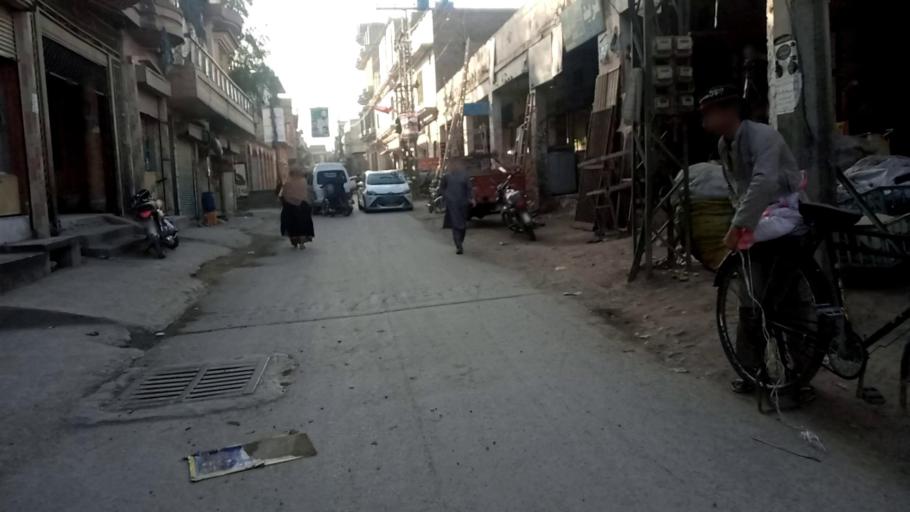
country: PK
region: Khyber Pakhtunkhwa
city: Peshawar
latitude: 34.0060
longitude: 71.6002
